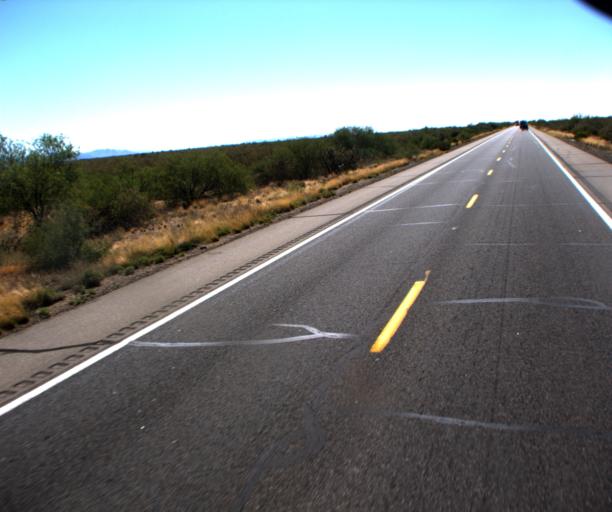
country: US
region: Arizona
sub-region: Yavapai County
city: Congress
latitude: 34.1612
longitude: -113.0049
